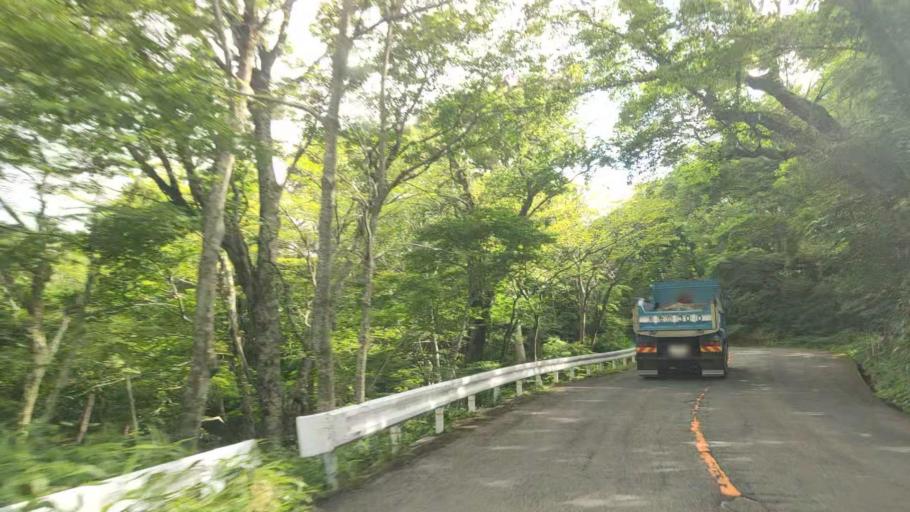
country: JP
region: Tottori
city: Yonago
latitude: 35.3842
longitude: 133.5254
